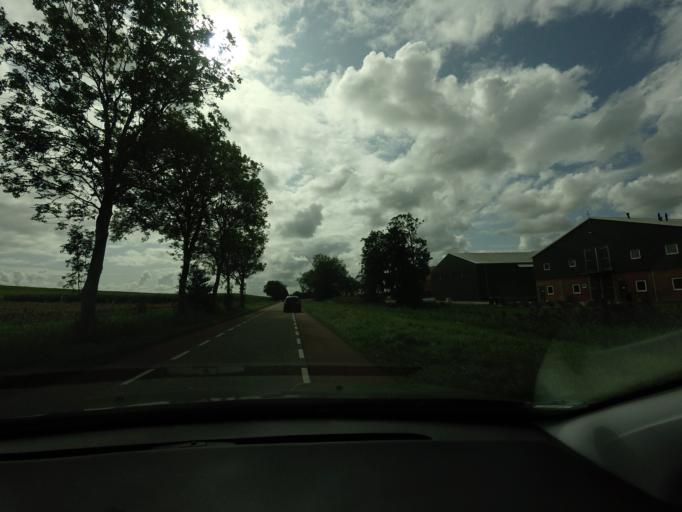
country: NL
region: North Holland
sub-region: Gemeente Medemblik
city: Medemblik
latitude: 52.8033
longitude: 5.1062
